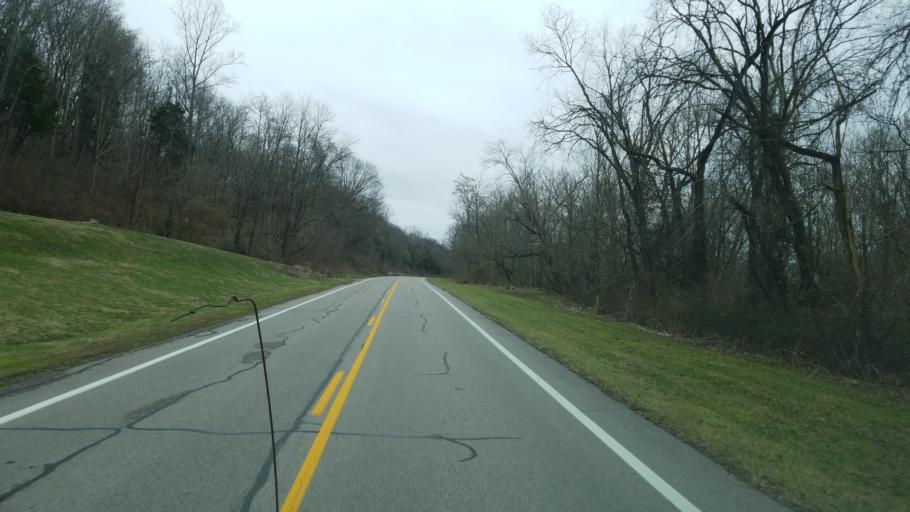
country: US
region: Kentucky
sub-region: Bracken County
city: Augusta
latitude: 38.7926
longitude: -84.1290
